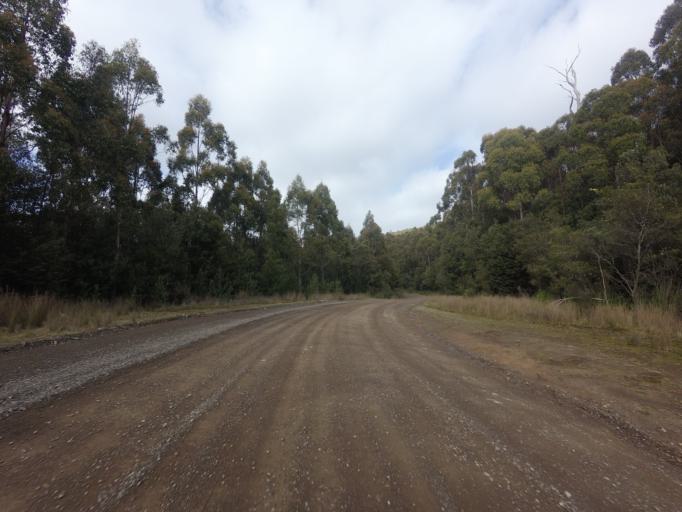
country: AU
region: Tasmania
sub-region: Huon Valley
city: Geeveston
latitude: -43.4765
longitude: 146.8923
